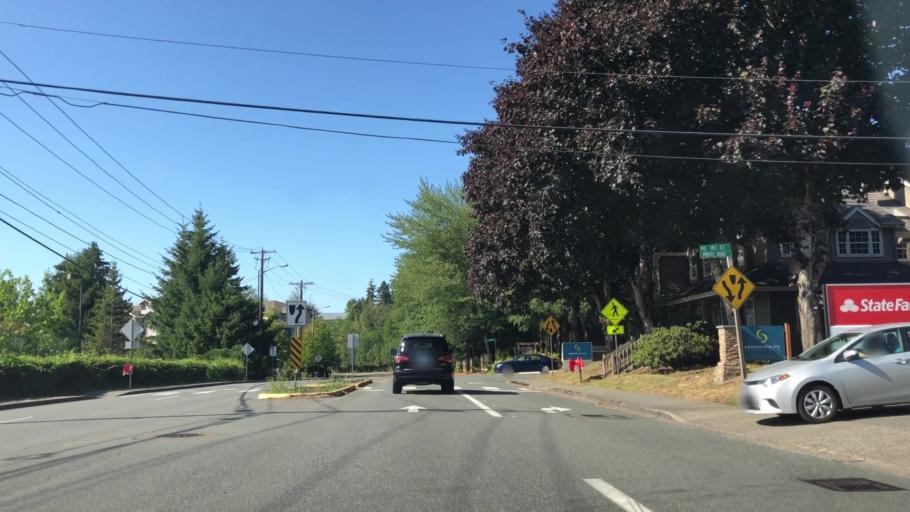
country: US
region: Washington
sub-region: King County
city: Woodinville
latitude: 47.7585
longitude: -122.1529
